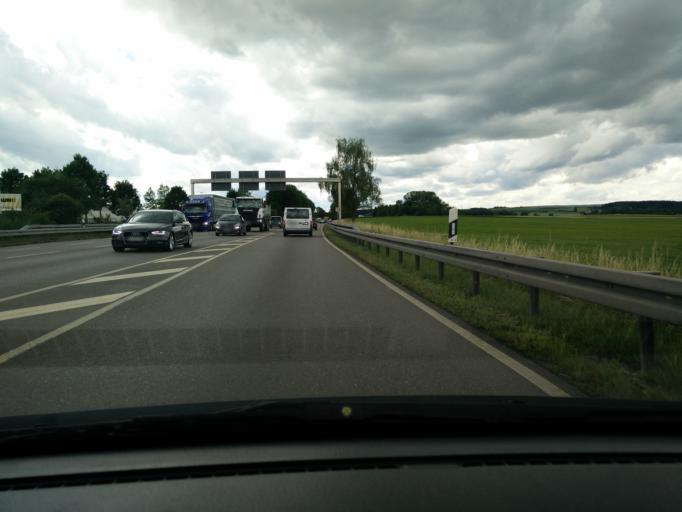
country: DE
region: Baden-Wuerttemberg
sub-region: Freiburg Region
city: Bad Durrheim
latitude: 48.0339
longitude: 8.5289
